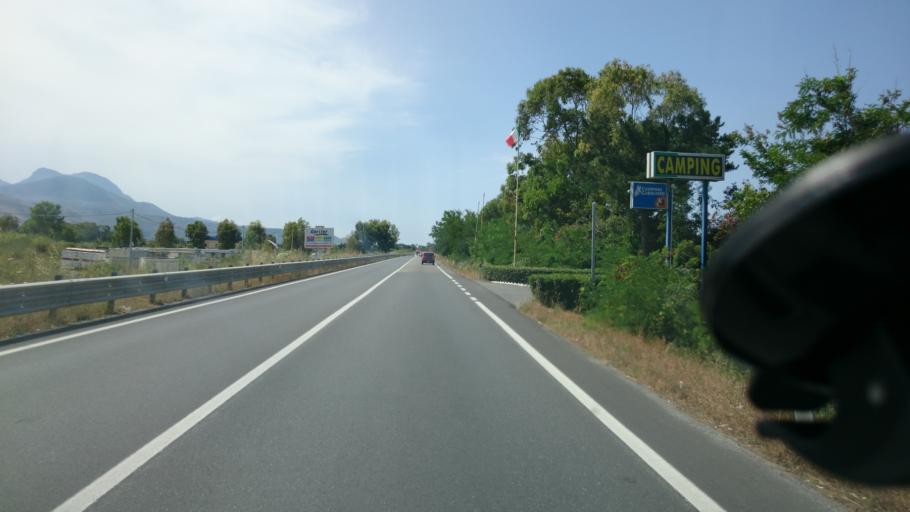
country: IT
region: Calabria
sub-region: Provincia di Cosenza
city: Scalea
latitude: 39.7890
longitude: 15.7941
